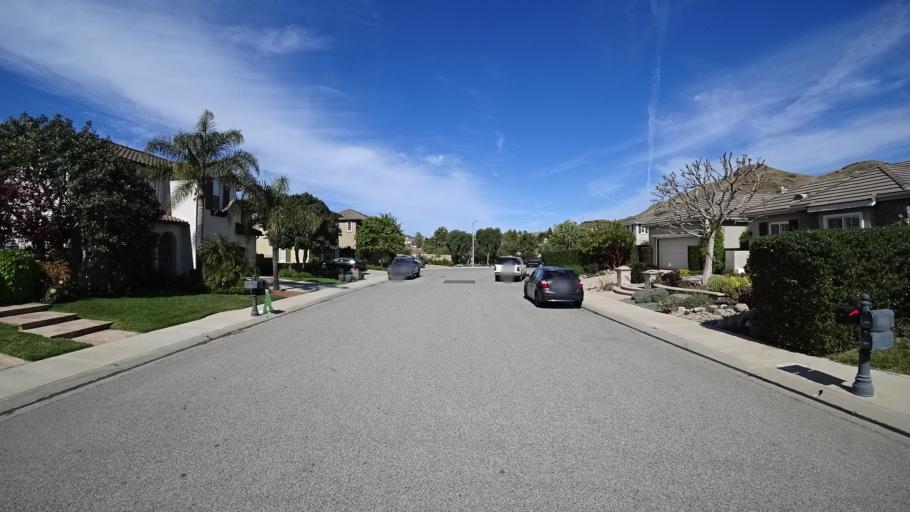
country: US
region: California
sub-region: Ventura County
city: Casa Conejo
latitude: 34.1741
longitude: -118.9711
